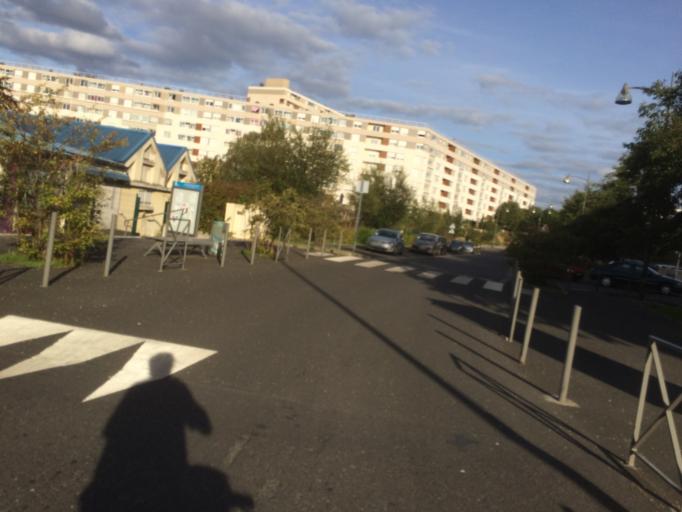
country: FR
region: Ile-de-France
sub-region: Departement de l'Essonne
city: Ballainvilliers
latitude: 48.6883
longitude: 2.2912
